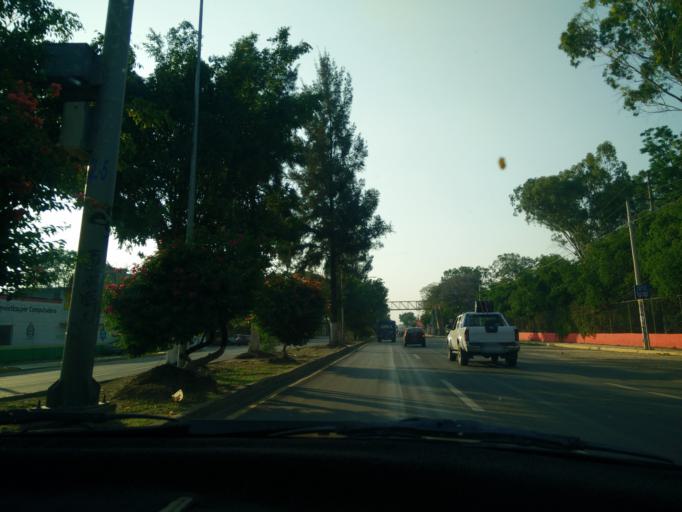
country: MX
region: Oaxaca
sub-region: Santa Maria Atzompa
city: San Jeronimo Yahuiche
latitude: 17.1173
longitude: -96.7600
